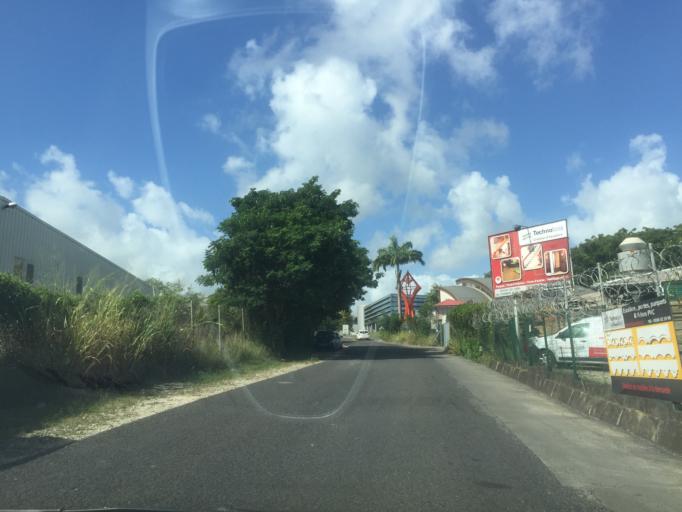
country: GP
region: Guadeloupe
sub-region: Guadeloupe
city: Baie-Mahault
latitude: 16.2418
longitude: -61.5818
